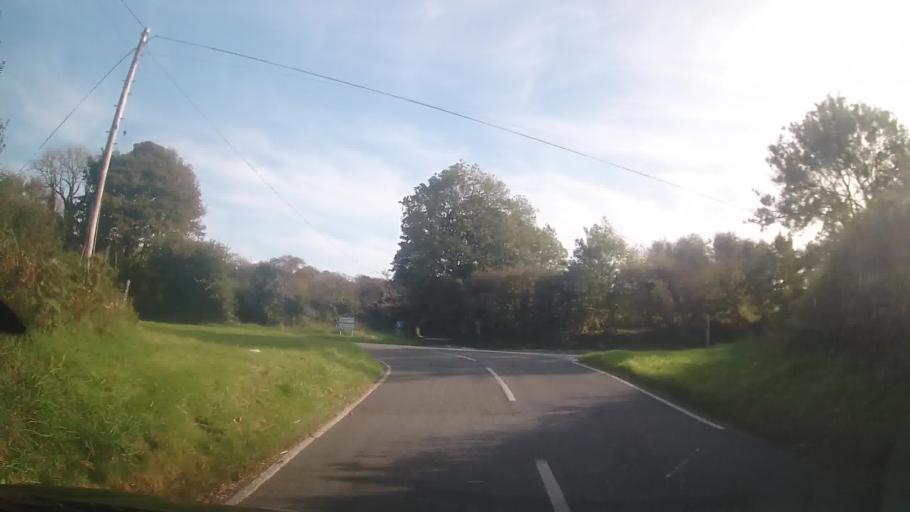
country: GB
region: Wales
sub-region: Pembrokeshire
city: Fishguard
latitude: 51.9761
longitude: -4.9255
